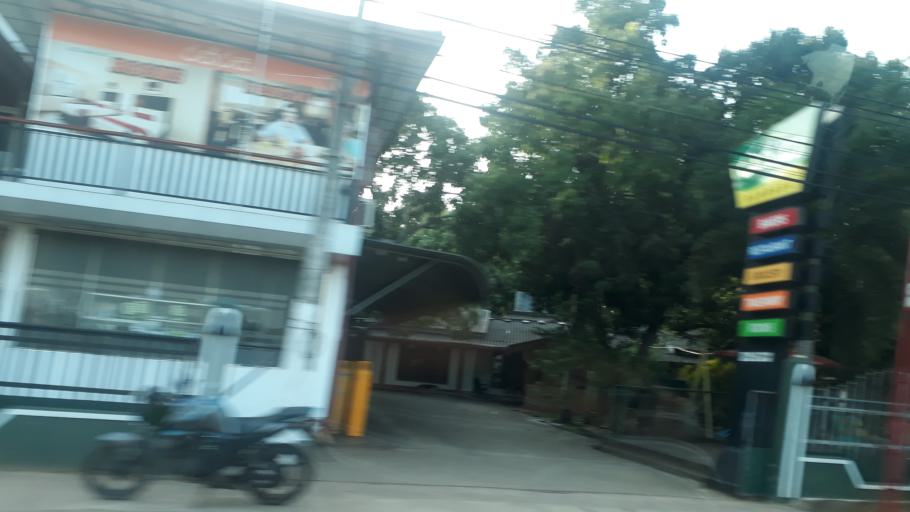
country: LK
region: North Central
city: Anuradhapura
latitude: 8.3047
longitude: 80.3774
